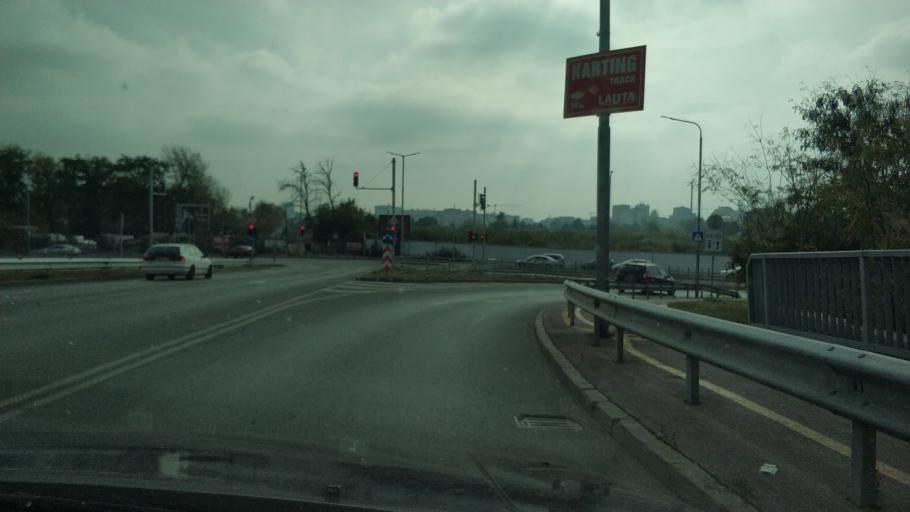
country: BG
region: Plovdiv
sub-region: Obshtina Plovdiv
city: Plovdiv
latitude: 42.1535
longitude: 24.7658
